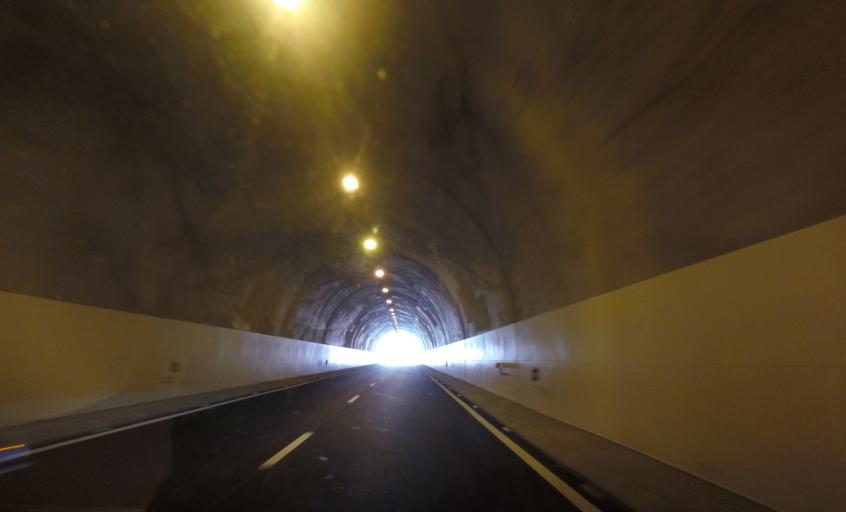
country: PT
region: Madeira
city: Camara de Lobos
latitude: 32.6657
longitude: -16.9696
